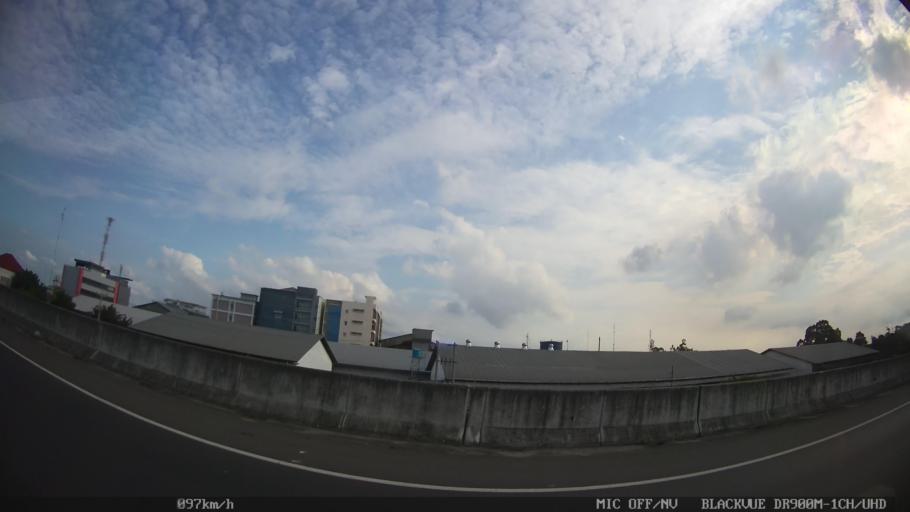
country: ID
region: North Sumatra
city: Medan
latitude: 3.6490
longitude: 98.6619
